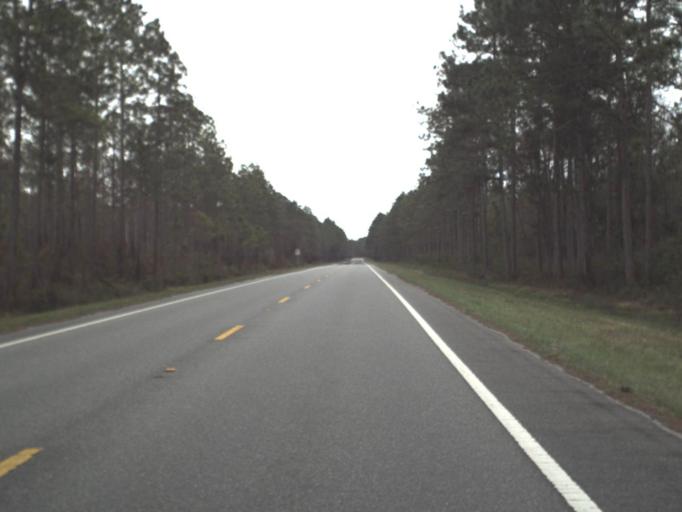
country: US
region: Florida
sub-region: Gadsden County
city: Midway
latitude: 30.3651
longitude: -84.5404
